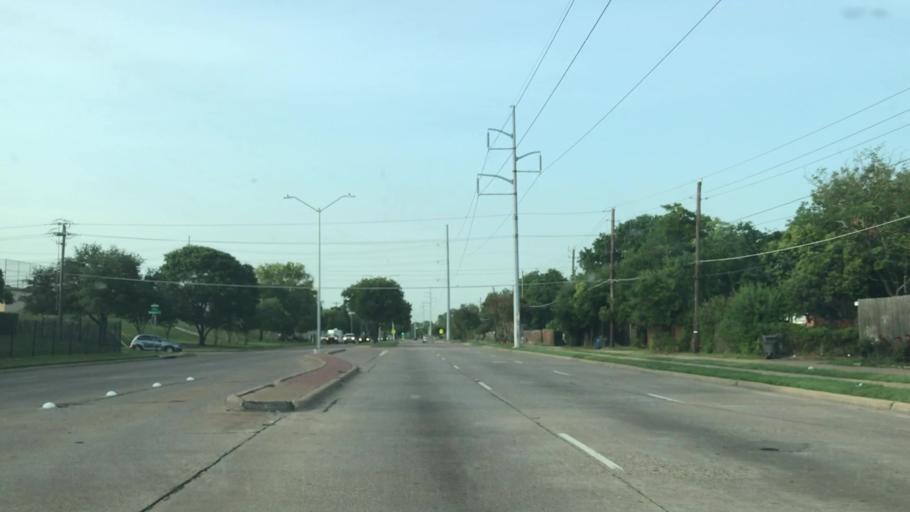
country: US
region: Texas
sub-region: Dallas County
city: Balch Springs
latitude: 32.7892
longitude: -96.7001
